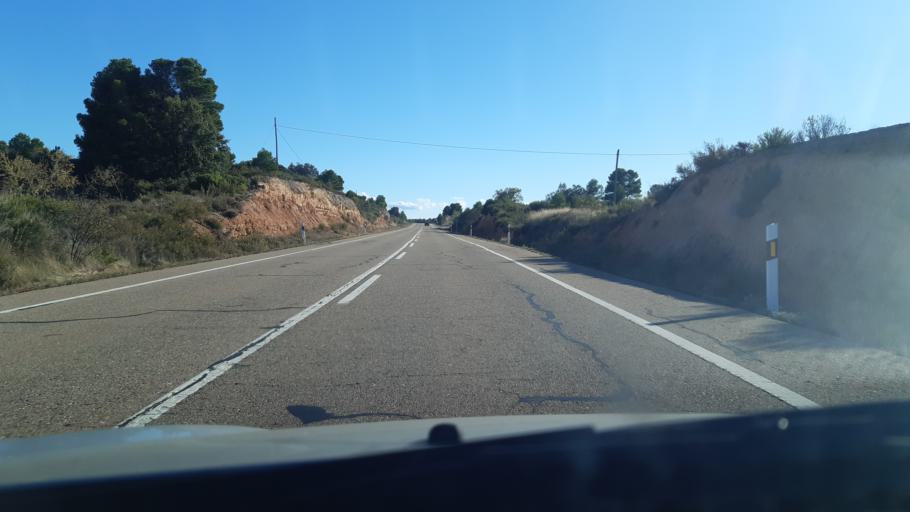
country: ES
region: Aragon
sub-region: Provincia de Teruel
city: Valdealgorfa
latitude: 40.9602
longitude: -0.0160
